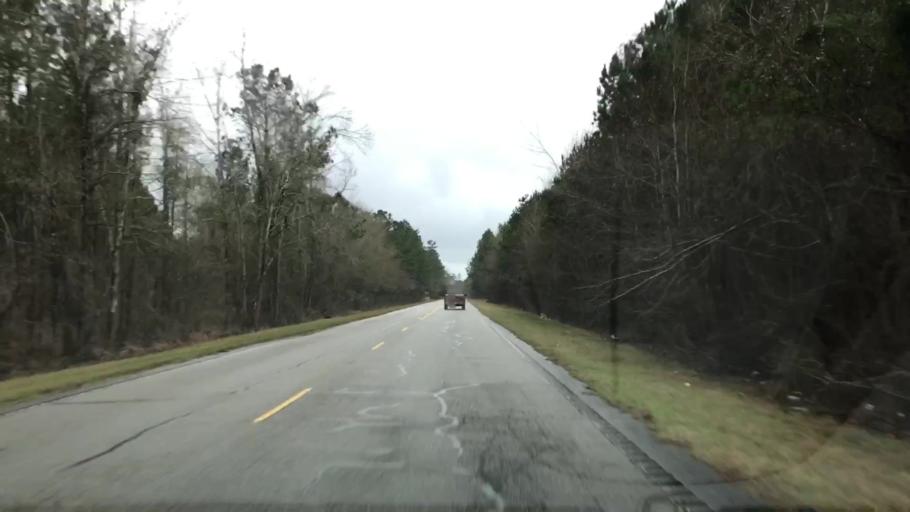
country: US
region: South Carolina
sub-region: Williamsburg County
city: Andrews
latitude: 33.5274
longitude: -79.4892
